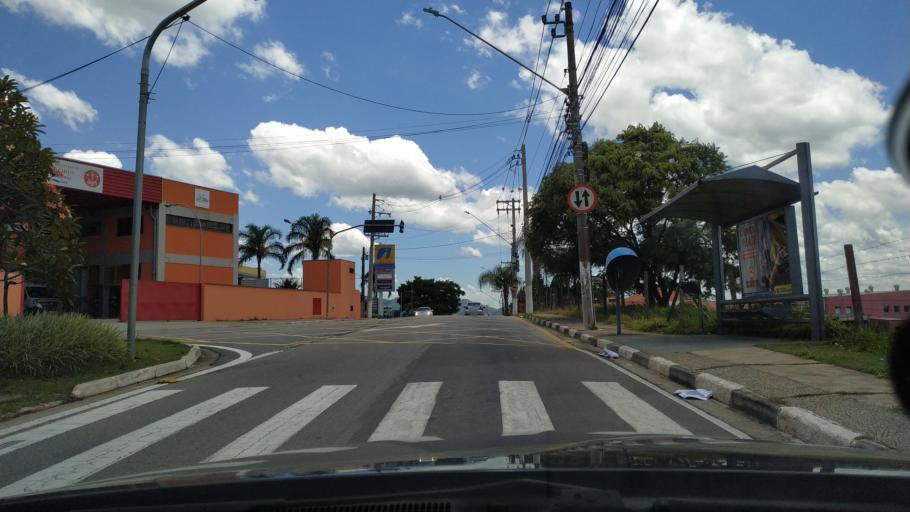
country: BR
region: Sao Paulo
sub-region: Santana De Parnaiba
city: Santana de Parnaiba
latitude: -23.4541
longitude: -46.8951
